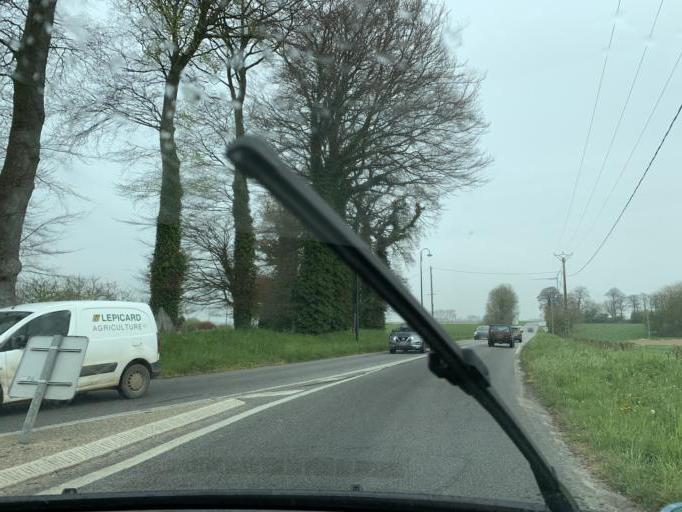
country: FR
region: Haute-Normandie
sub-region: Departement de la Seine-Maritime
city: Bertheauville
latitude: 49.7830
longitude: 0.5939
